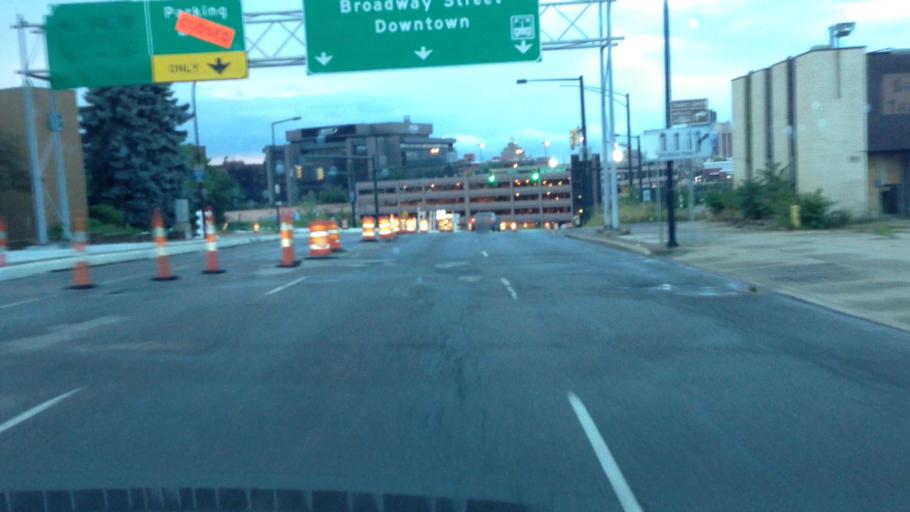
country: US
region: Ohio
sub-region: Summit County
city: Akron
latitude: 41.0680
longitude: -81.5244
